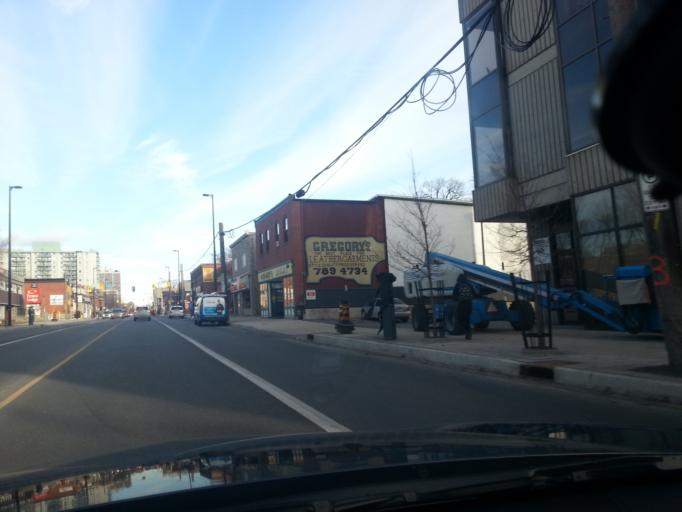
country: CA
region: Ontario
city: Ottawa
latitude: 45.4308
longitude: -75.6807
